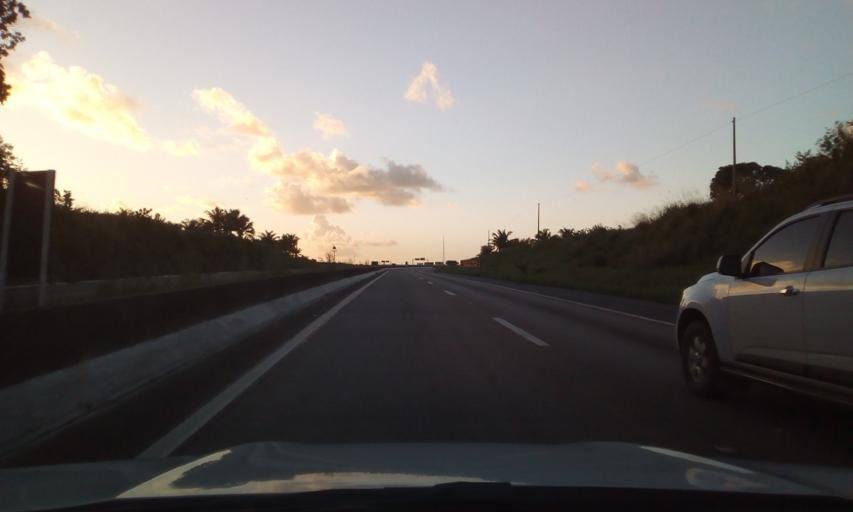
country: BR
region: Pernambuco
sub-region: Itapissuma
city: Itapissuma
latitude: -7.6792
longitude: -34.9267
